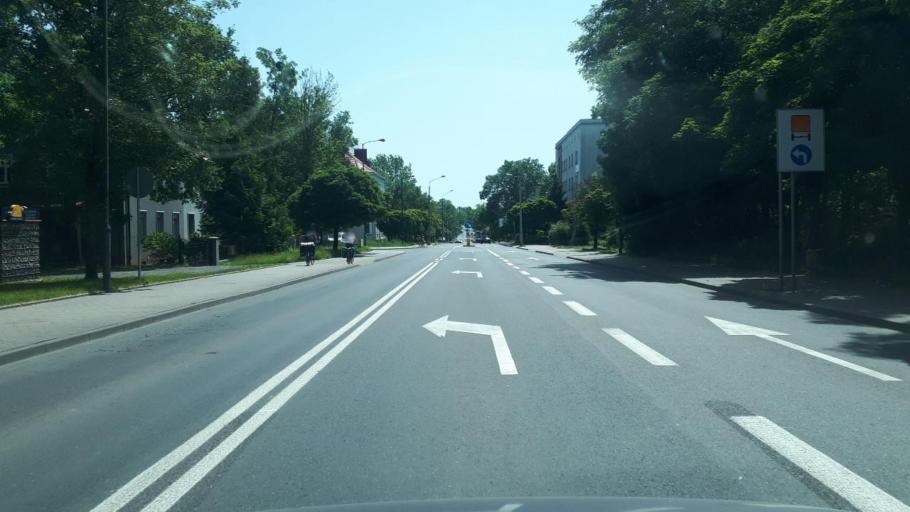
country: PL
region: Silesian Voivodeship
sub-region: Gliwice
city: Gliwice
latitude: 50.3145
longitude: 18.6672
